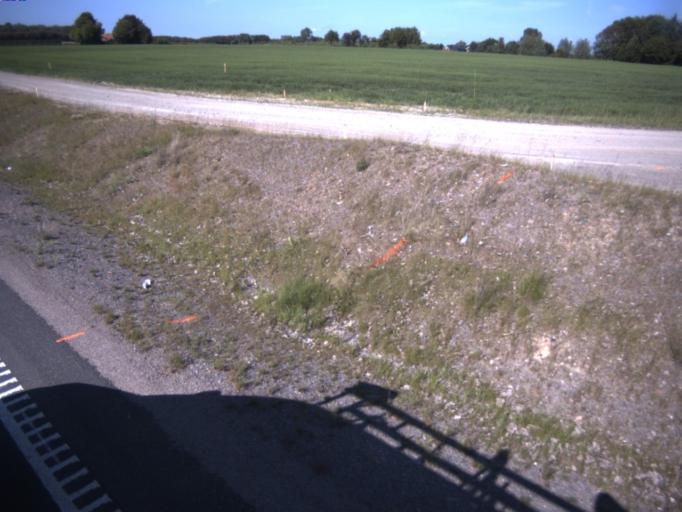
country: SE
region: Skane
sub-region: Helsingborg
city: Odakra
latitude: 56.0511
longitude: 12.7531
